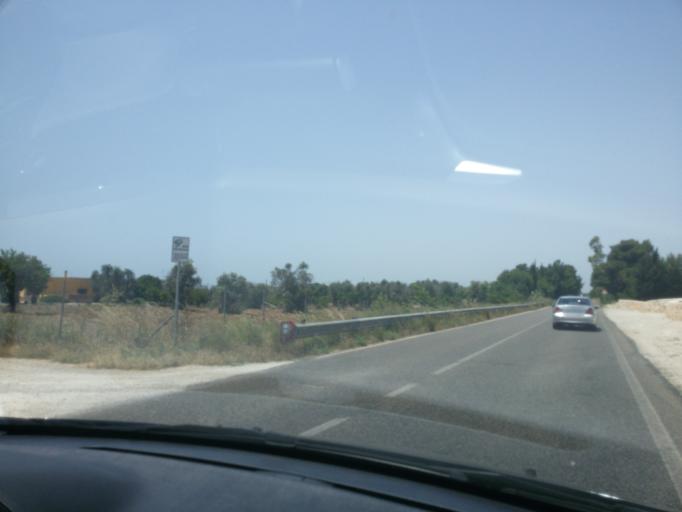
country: IT
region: Apulia
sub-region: Provincia di Lecce
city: Porto Cesareo
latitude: 40.2696
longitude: 17.9075
